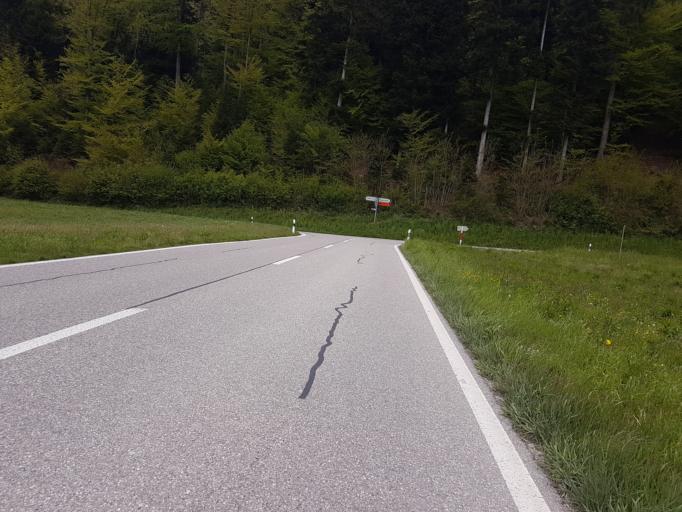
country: CH
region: Bern
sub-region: Oberaargau
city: Niederbipp
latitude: 47.2322
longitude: 7.7069
